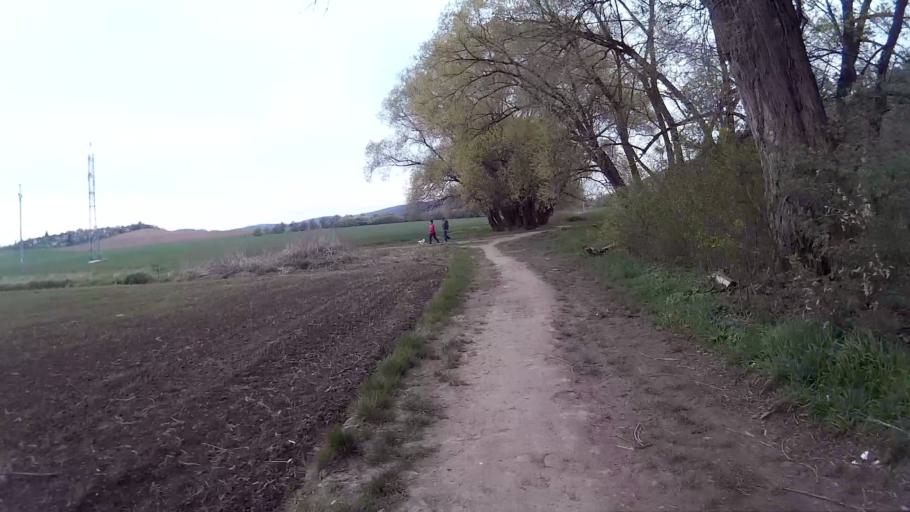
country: CZ
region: South Moravian
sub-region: Mesto Brno
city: Mokra Hora
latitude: 49.2269
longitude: 16.5615
